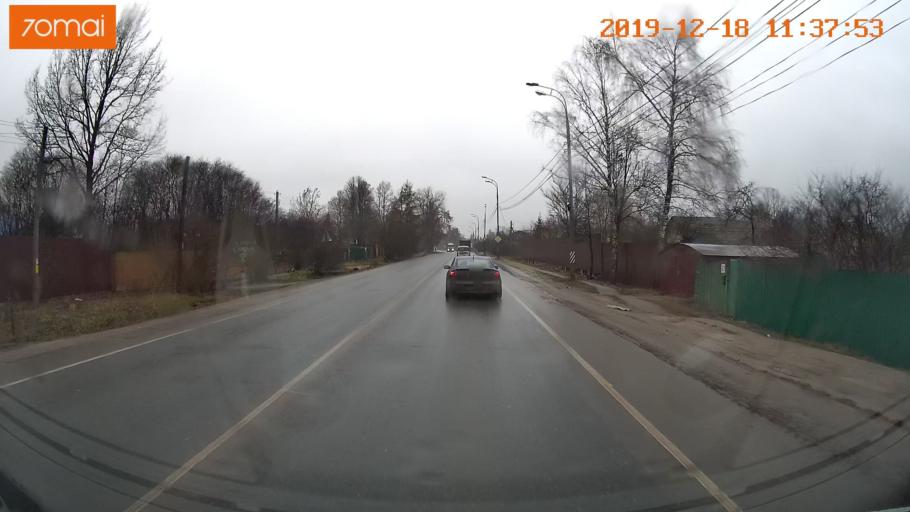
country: RU
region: Moskovskaya
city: Zvenigorod
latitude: 55.6931
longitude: 36.8922
